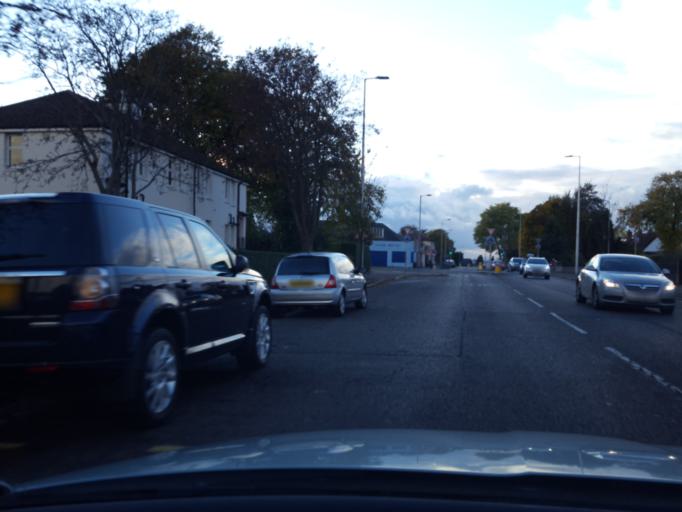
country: GB
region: Scotland
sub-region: Dundee City
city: Dundee
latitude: 56.4746
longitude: -2.9927
